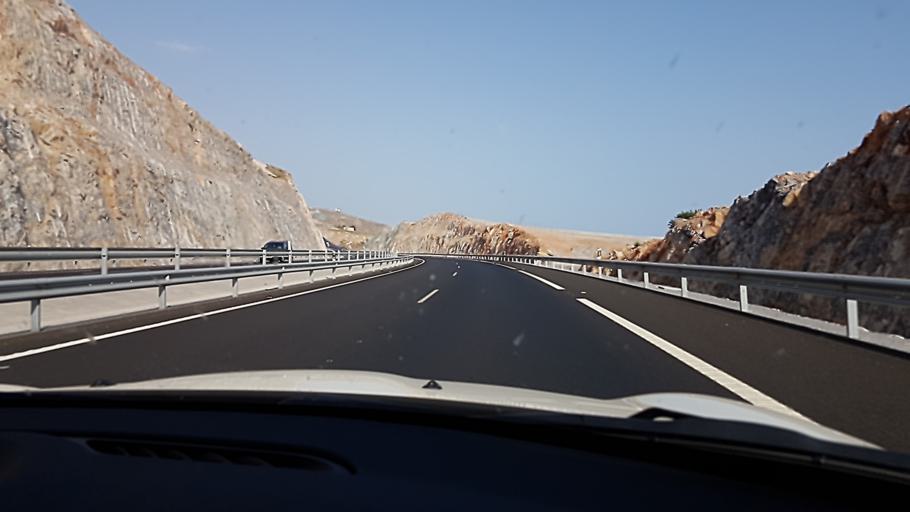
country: ES
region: Andalusia
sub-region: Provincia de Granada
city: Gualchos
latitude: 36.7097
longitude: -3.4107
